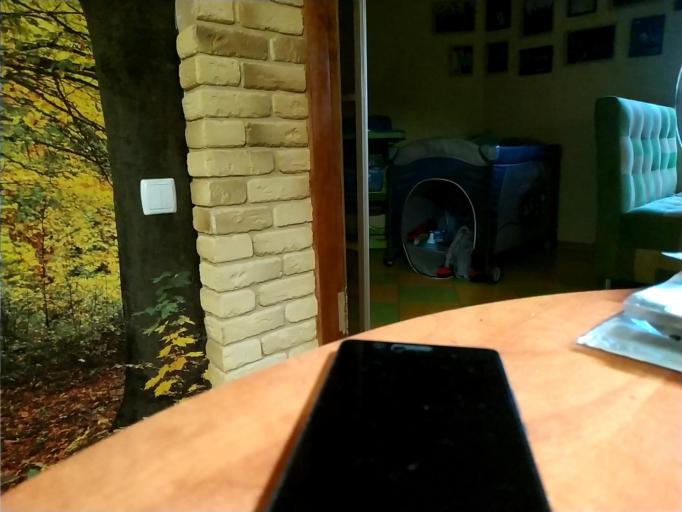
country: RU
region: Orjol
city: Znamenskoye
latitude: 53.4492
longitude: 35.5266
